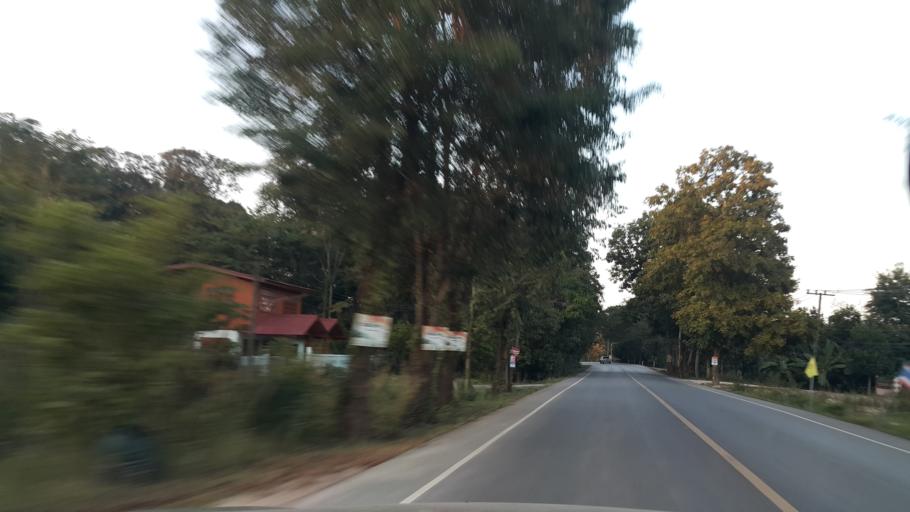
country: TH
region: Phrae
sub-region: Amphoe Wang Chin
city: Wang Chin
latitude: 17.8656
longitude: 99.6223
